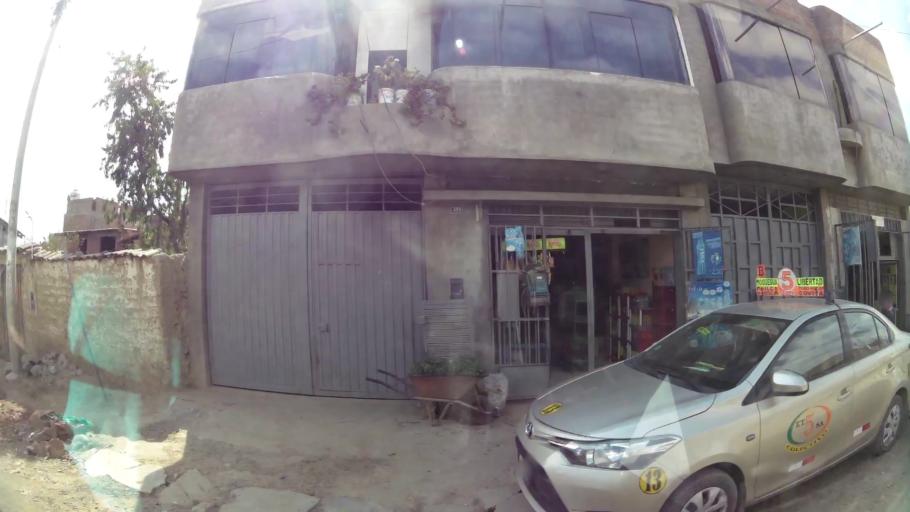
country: PE
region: Junin
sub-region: Provincia de Huancayo
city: Huancayo
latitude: -12.0956
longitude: -75.2014
